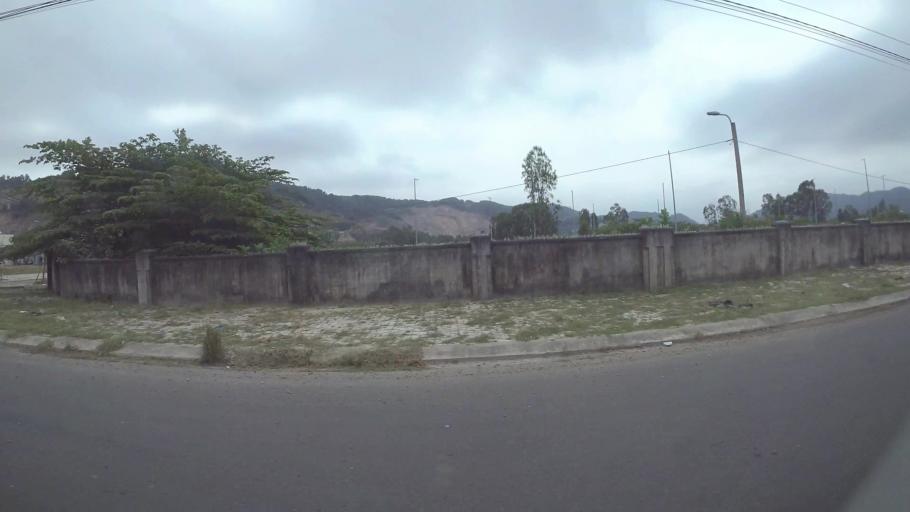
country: VN
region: Da Nang
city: Lien Chieu
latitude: 16.0460
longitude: 108.1649
